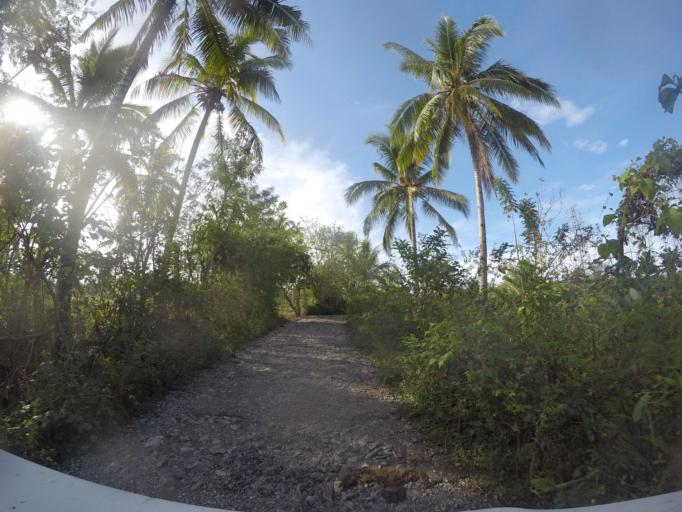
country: TL
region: Baucau
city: Baucau
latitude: -8.4921
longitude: 126.4536
